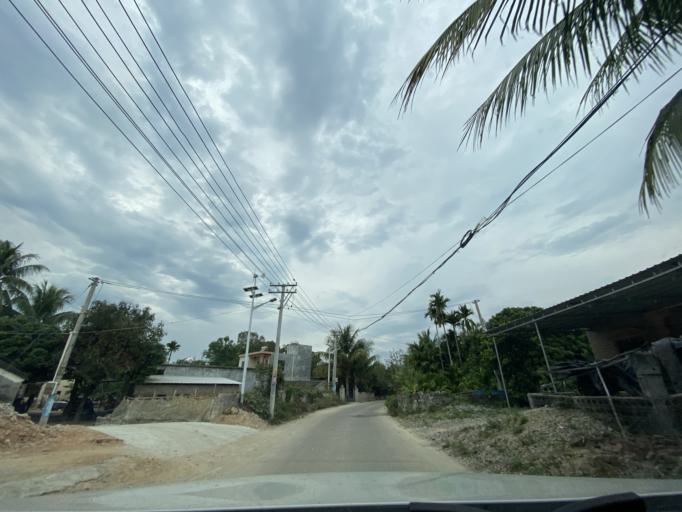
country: CN
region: Hainan
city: Yingzhou
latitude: 18.4063
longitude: 109.8183
